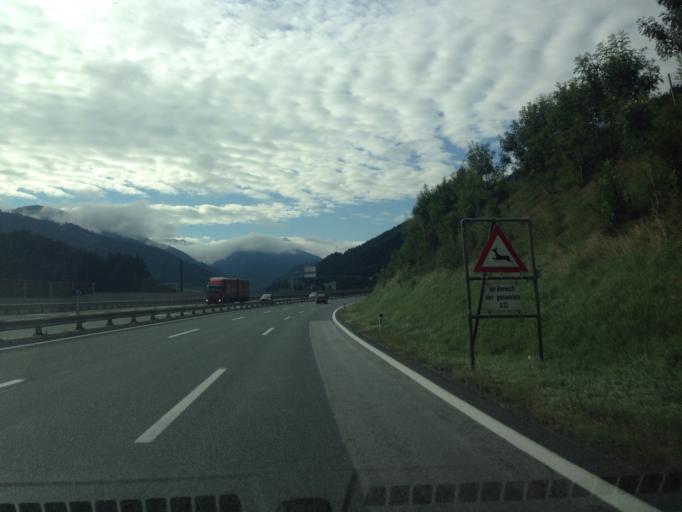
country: AT
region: Tyrol
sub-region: Politischer Bezirk Innsbruck Land
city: Matrei am Brenner
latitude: 47.1174
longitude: 11.4501
